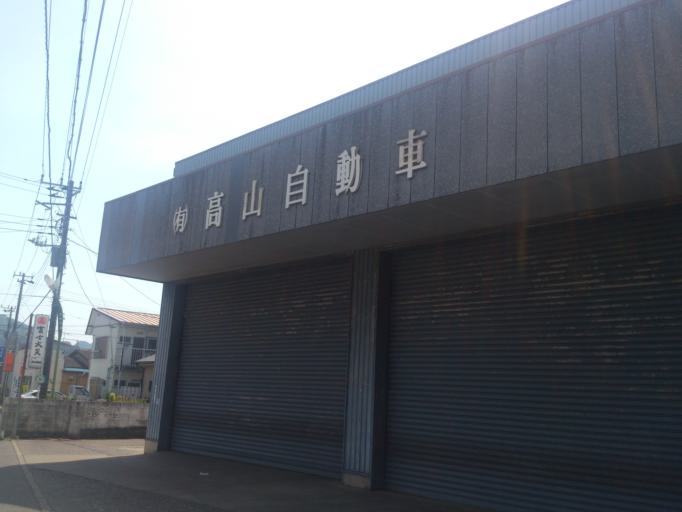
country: JP
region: Chiba
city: Tateyama
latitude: 35.0898
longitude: 139.8483
